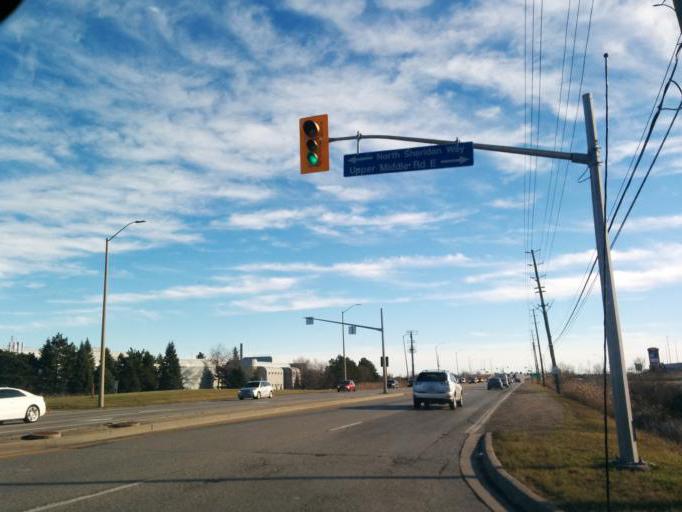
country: CA
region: Ontario
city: Oakville
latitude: 43.5133
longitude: -79.6689
